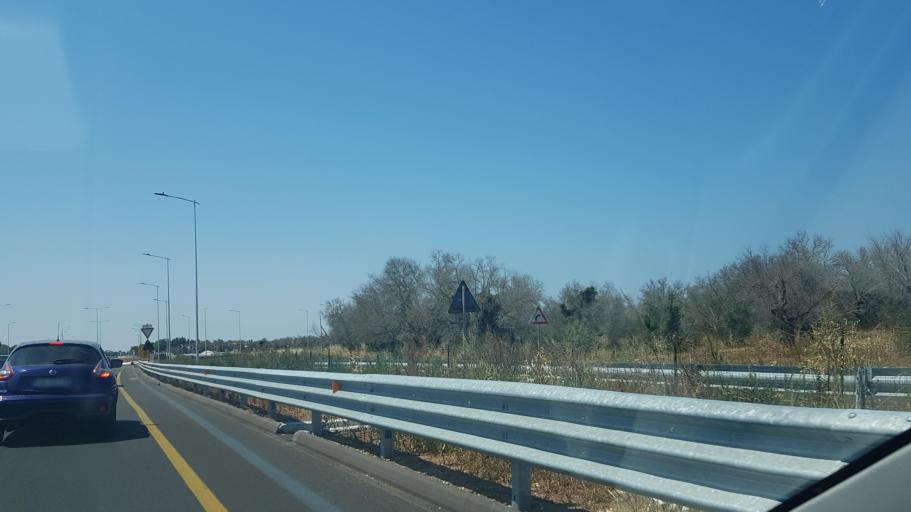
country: IT
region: Apulia
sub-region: Provincia di Lecce
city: Struda
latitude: 40.3239
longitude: 18.2617
